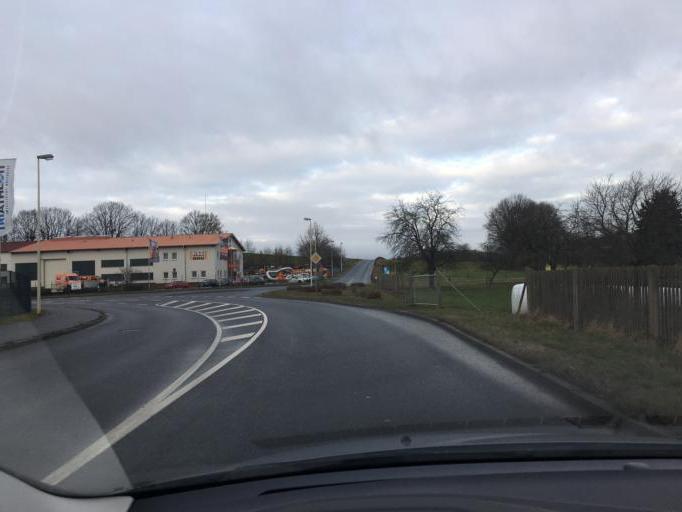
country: DE
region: Saxony
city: Pfaffroda
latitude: 50.8379
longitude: 12.5232
